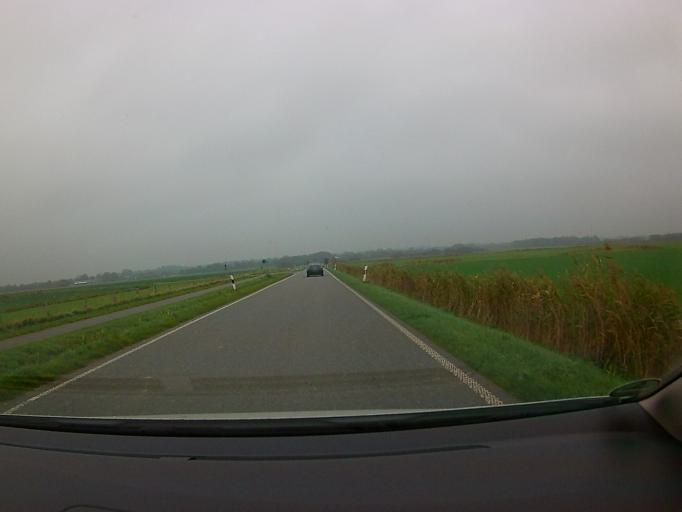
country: DE
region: Schleswig-Holstein
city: Bordelum
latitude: 54.6304
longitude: 8.9086
